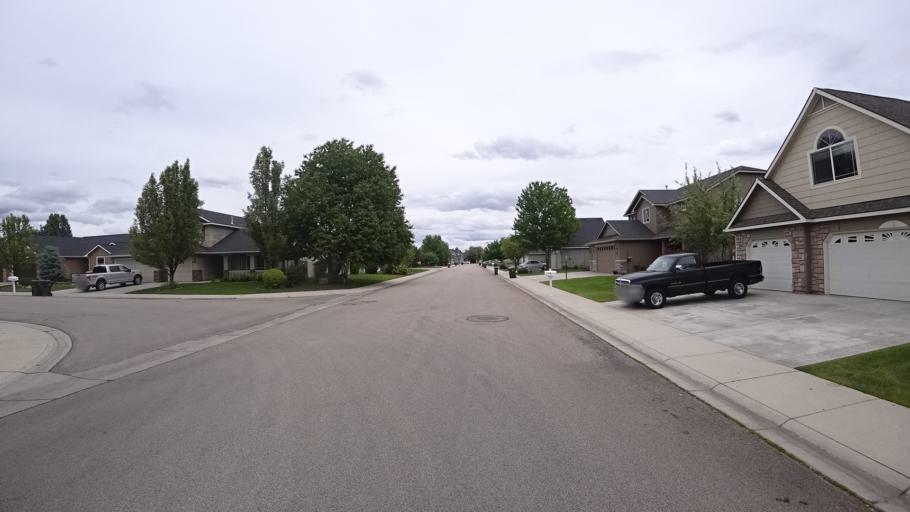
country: US
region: Idaho
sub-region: Ada County
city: Meridian
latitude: 43.6385
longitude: -116.4034
